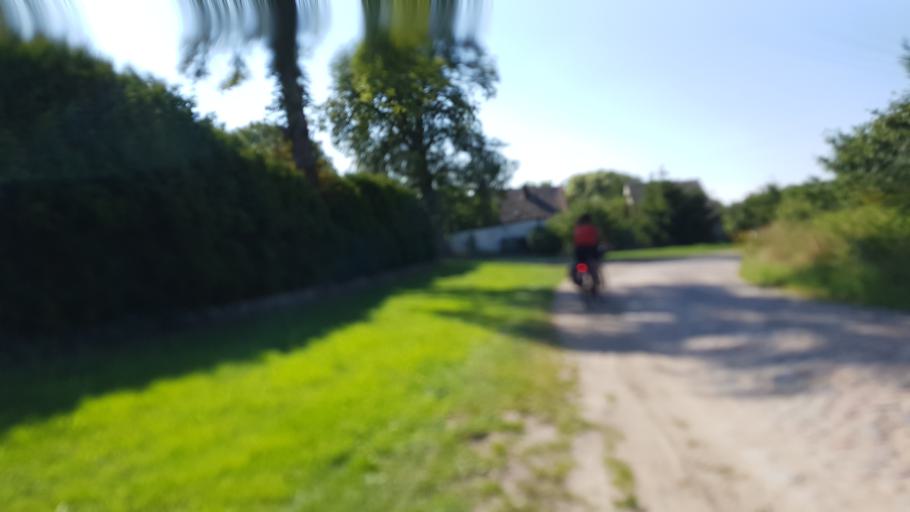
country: PL
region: West Pomeranian Voivodeship
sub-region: Powiat gryfinski
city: Gryfino
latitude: 53.1485
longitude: 14.5068
